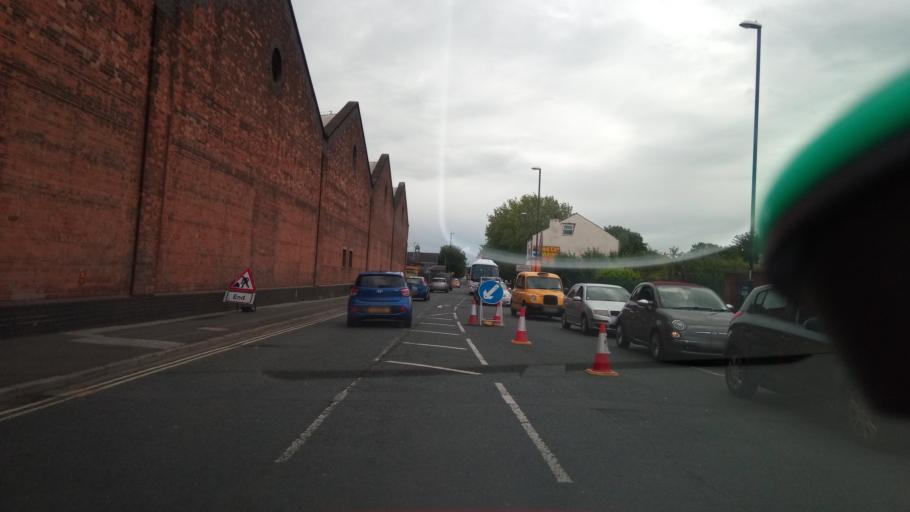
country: GB
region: England
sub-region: Derby
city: Derby
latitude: 52.9057
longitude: -1.4626
